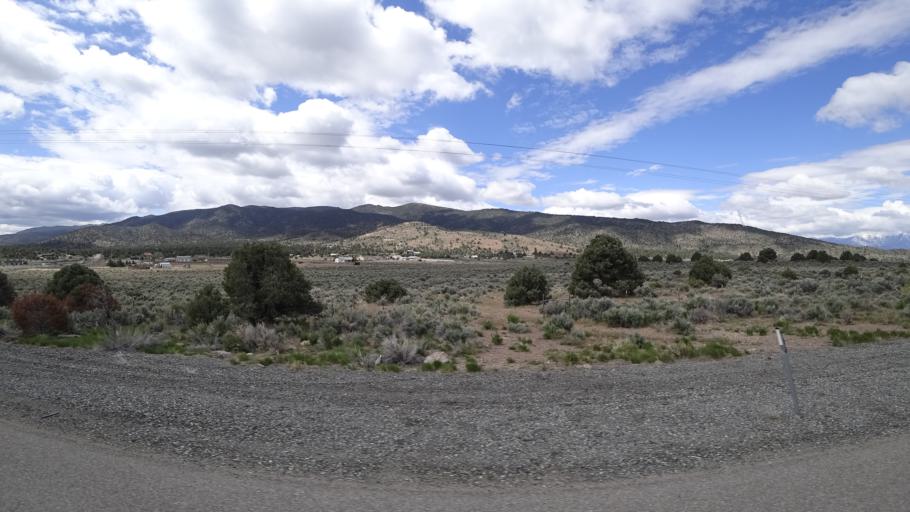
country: US
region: Nevada
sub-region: Douglas County
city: Gardnerville Ranchos
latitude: 38.7828
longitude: -119.5890
